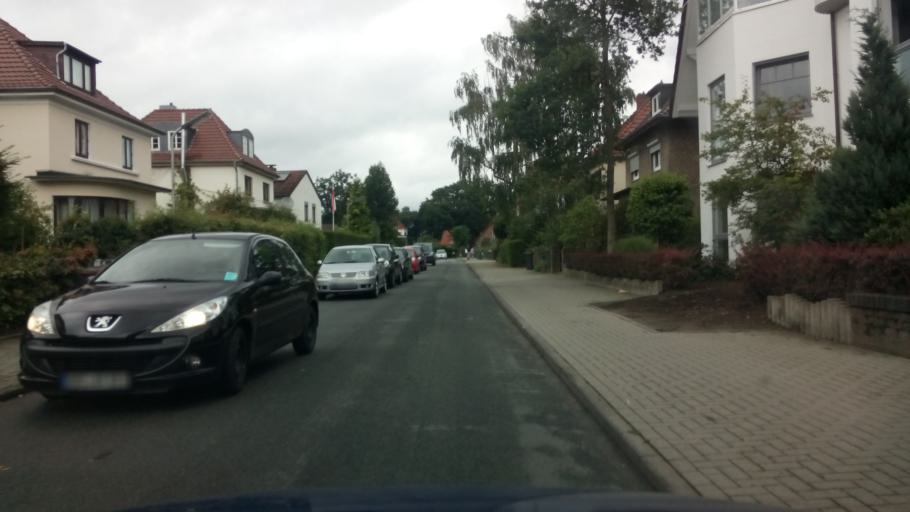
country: DE
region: Lower Saxony
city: Lemwerder
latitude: 53.1761
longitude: 8.6286
